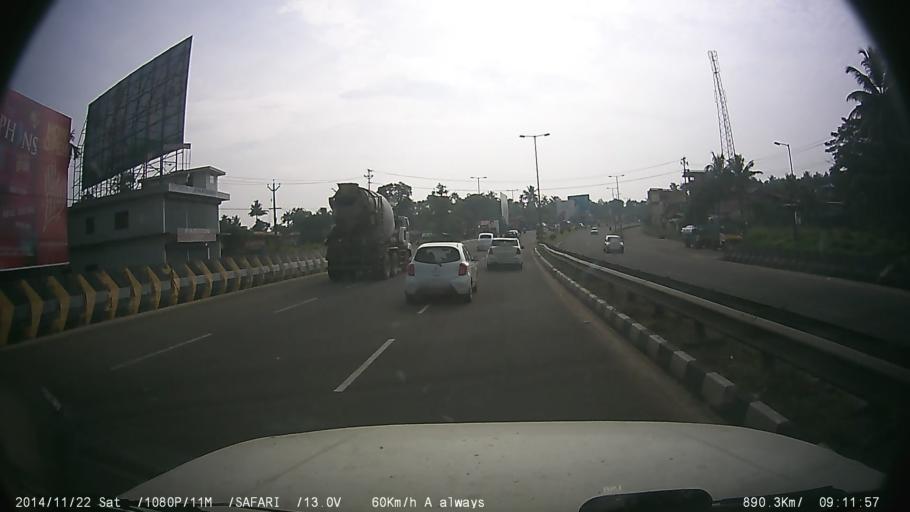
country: IN
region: Kerala
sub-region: Thrissur District
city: Kizhake Chalakudi
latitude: 10.2877
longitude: 76.3397
